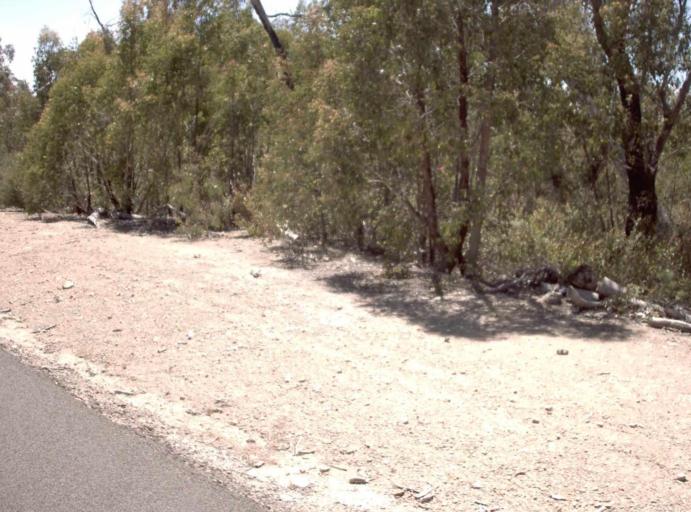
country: AU
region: New South Wales
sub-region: Snowy River
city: Jindabyne
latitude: -37.1244
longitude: 148.2483
